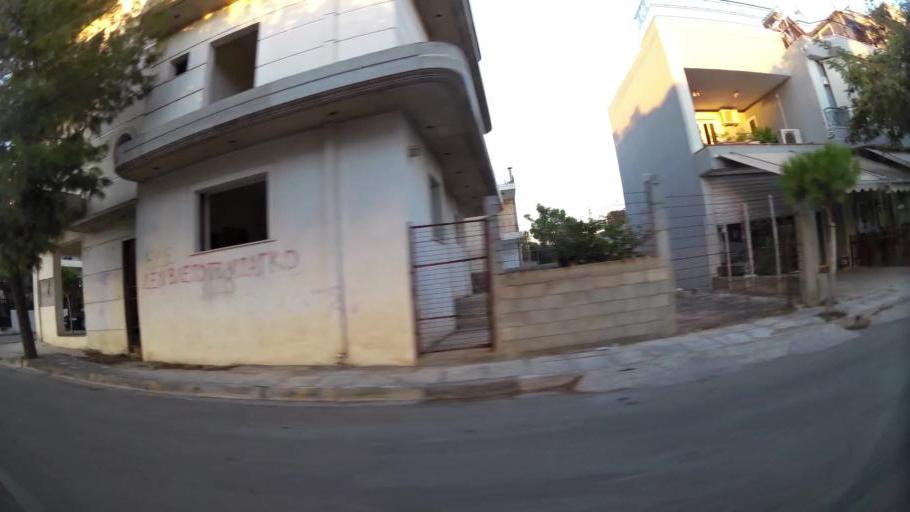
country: GR
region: Attica
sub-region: Nomarchia Dytikis Attikis
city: Ano Liosia
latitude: 38.0868
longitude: 23.6974
